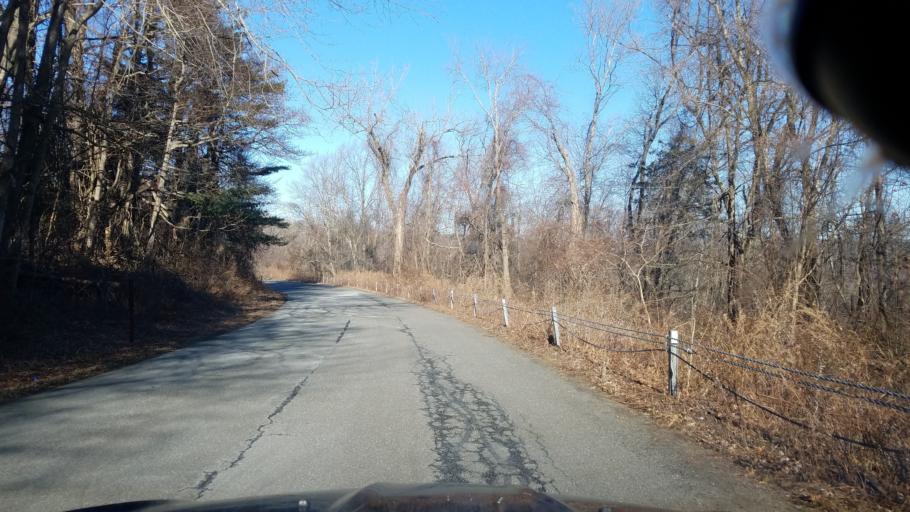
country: US
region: Connecticut
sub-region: New Haven County
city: Heritage Village
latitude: 41.4959
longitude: -73.2712
